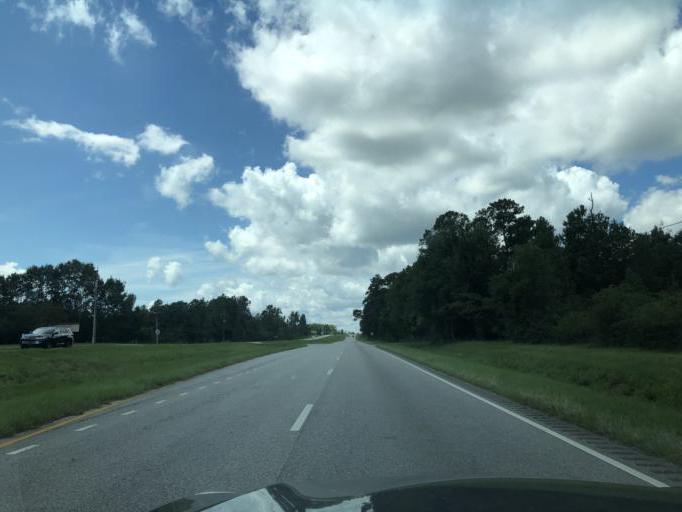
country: US
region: Alabama
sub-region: Barbour County
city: Eufaula
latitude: 31.9553
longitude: -85.1214
